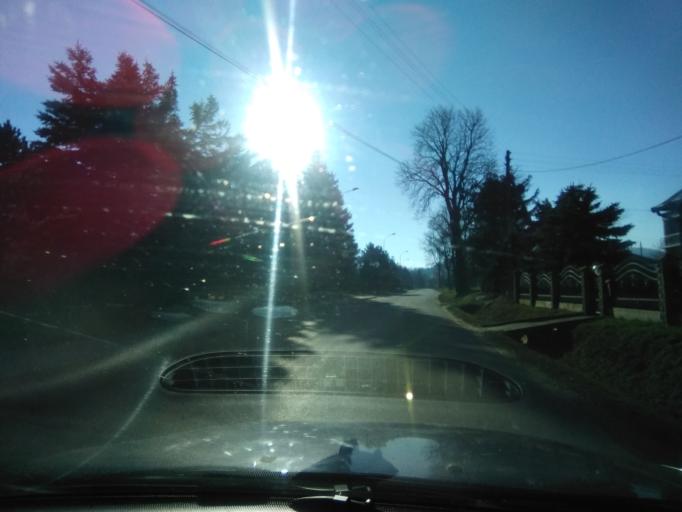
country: PL
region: Subcarpathian Voivodeship
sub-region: Powiat krosnienski
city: Rymanow
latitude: 49.5830
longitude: 21.8658
